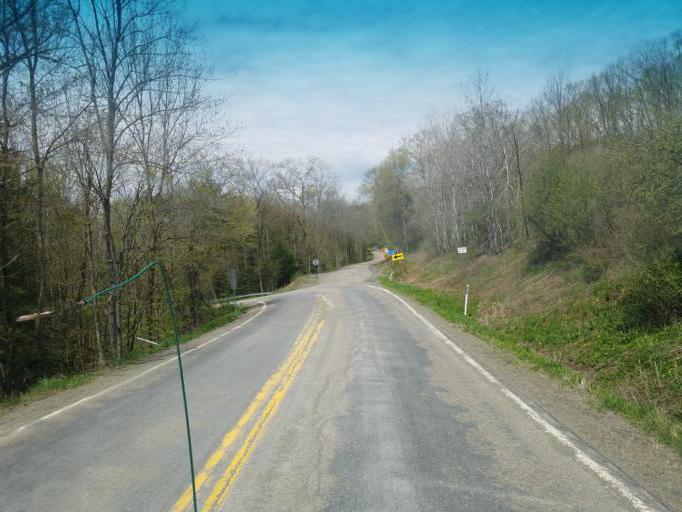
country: US
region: Pennsylvania
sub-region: Tioga County
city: Wellsboro
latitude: 41.7001
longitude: -77.4389
